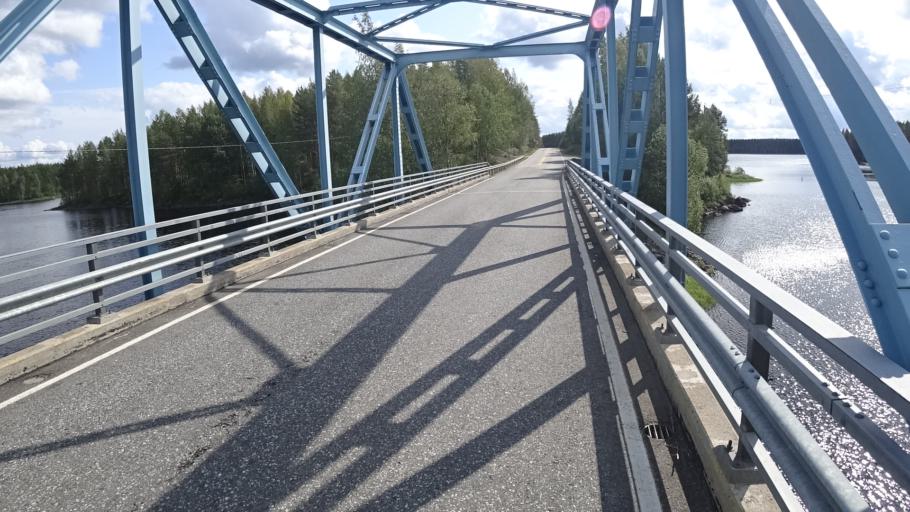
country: FI
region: North Karelia
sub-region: Joensuu
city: Ilomantsi
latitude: 62.6217
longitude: 31.1983
